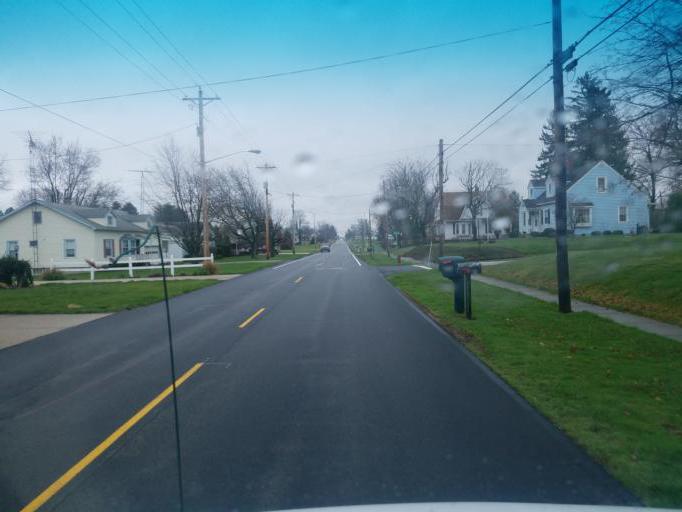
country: US
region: Ohio
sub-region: Huron County
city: Willard
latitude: 40.9605
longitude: -82.8473
